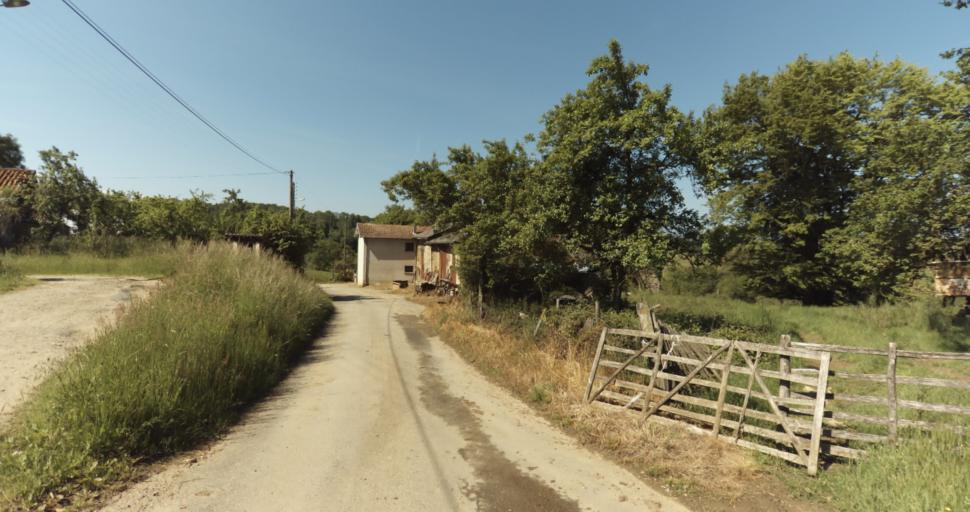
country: FR
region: Limousin
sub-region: Departement de la Haute-Vienne
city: Le Vigen
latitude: 45.7111
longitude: 1.2872
